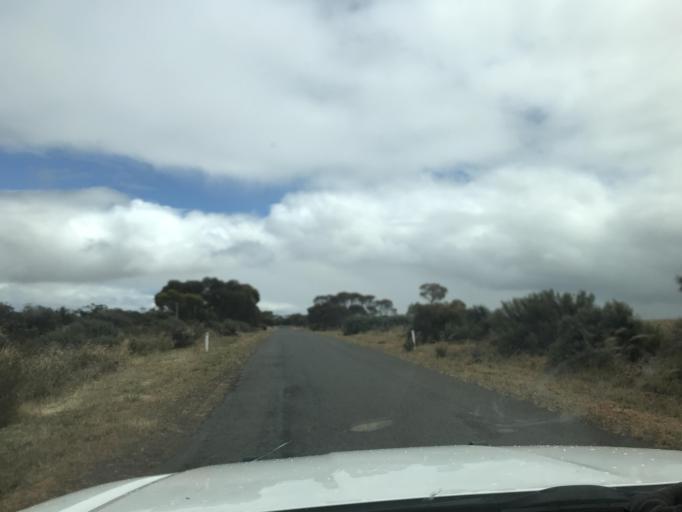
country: AU
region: South Australia
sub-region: Tatiara
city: Bordertown
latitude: -36.1418
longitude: 141.2255
